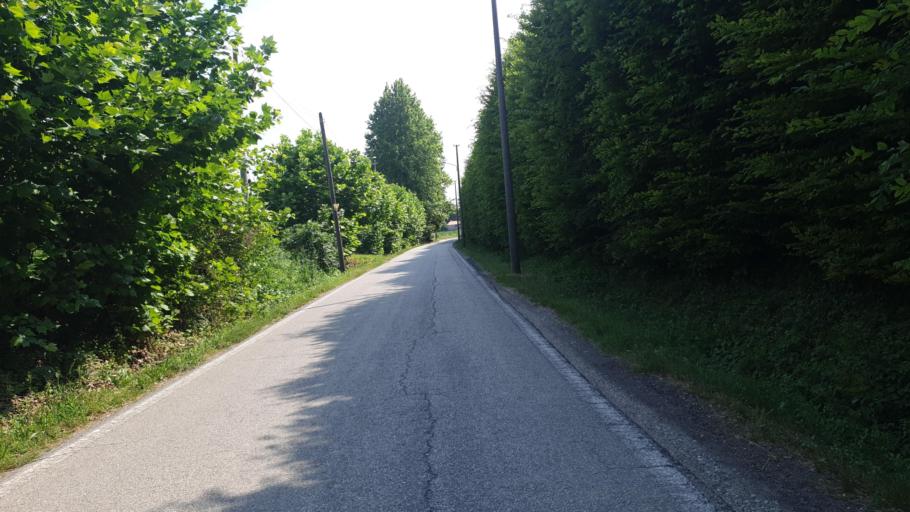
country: IT
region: Veneto
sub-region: Provincia di Padova
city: Tencarola
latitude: 45.3797
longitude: 11.8123
